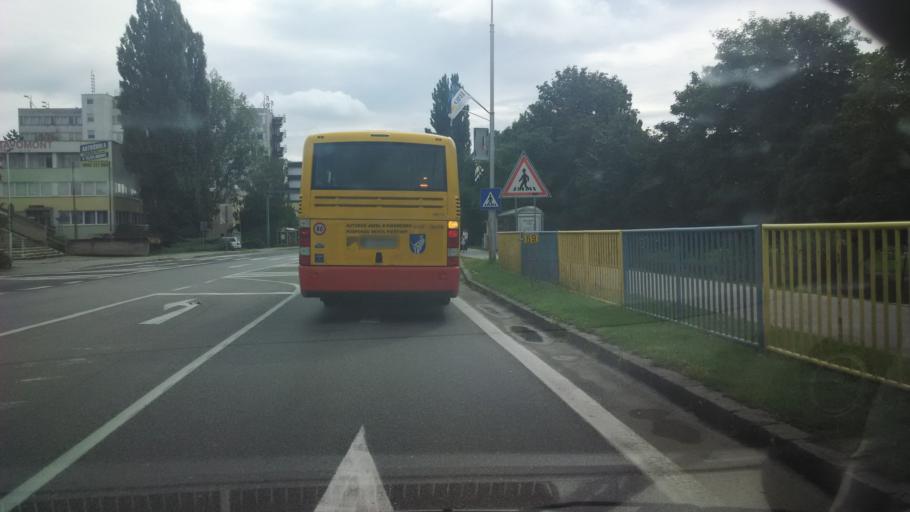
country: SK
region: Trnavsky
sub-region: Okres Trnava
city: Piestany
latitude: 48.5876
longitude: 17.8194
